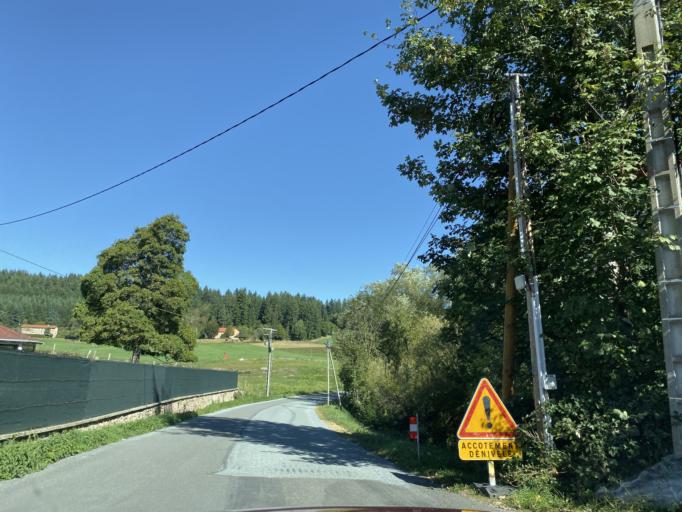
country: FR
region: Rhone-Alpes
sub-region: Departement de la Loire
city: Noiretable
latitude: 45.8213
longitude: 3.7691
